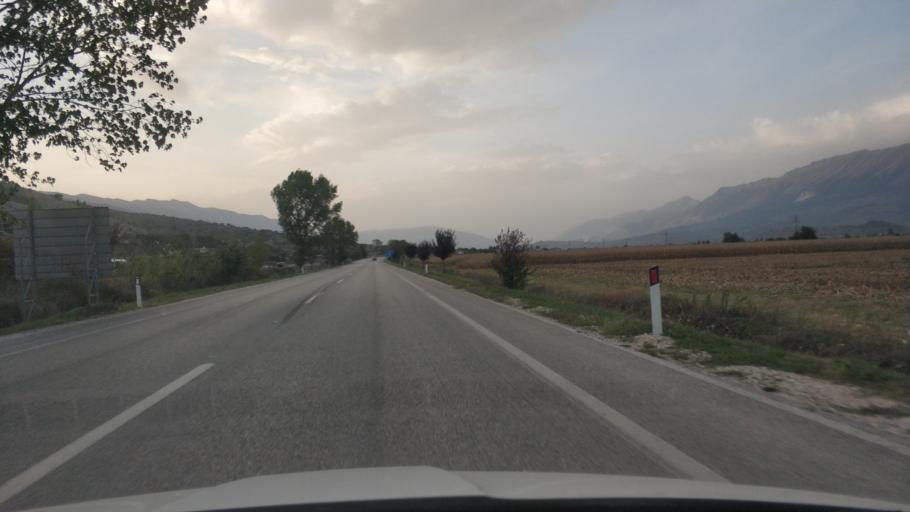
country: AL
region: Gjirokaster
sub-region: Rrethi i Gjirokastres
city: Libohove
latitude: 39.9895
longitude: 20.2209
